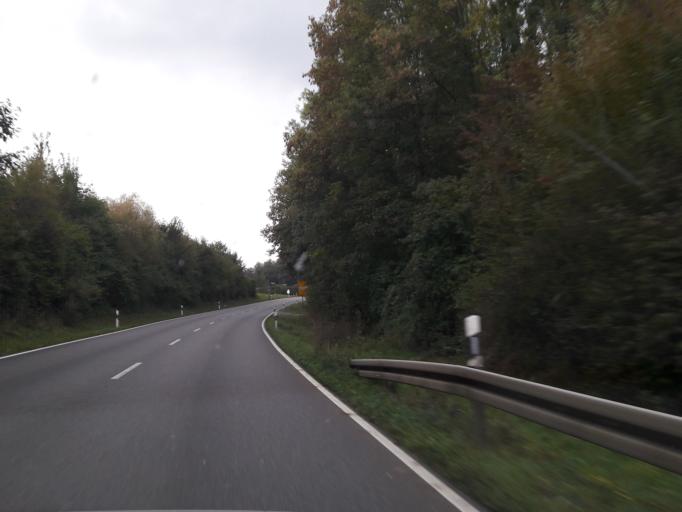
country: DE
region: Baden-Wuerttemberg
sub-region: Regierungsbezirk Stuttgart
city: Mockmuhl
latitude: 49.2910
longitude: 9.3665
